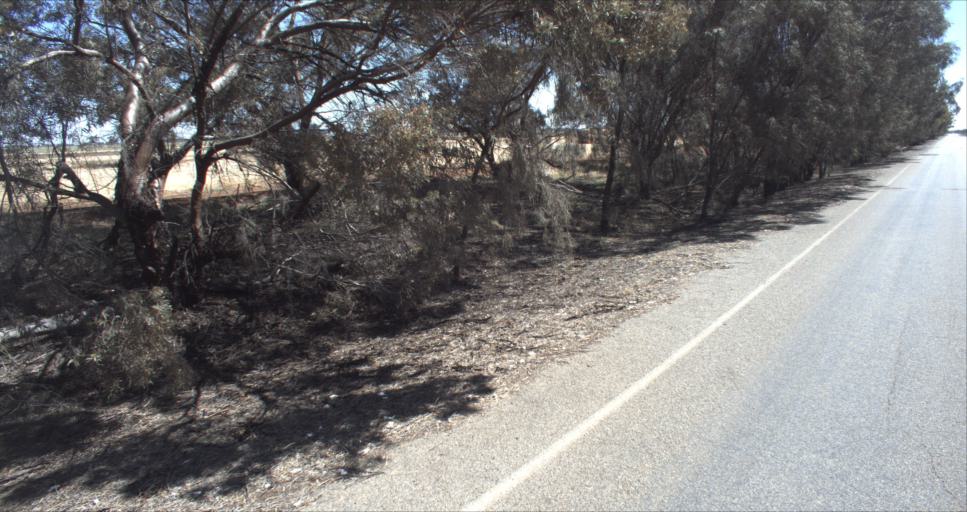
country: AU
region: New South Wales
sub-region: Leeton
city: Leeton
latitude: -34.4712
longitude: 146.2923
